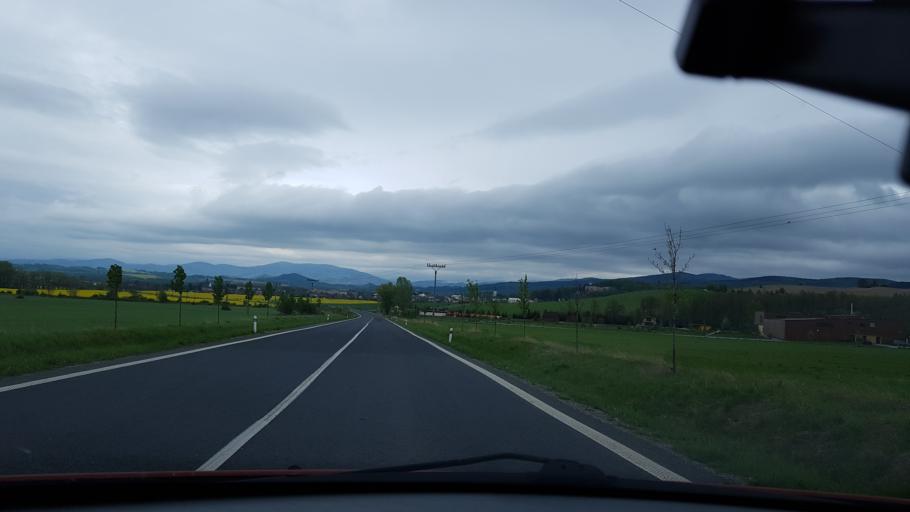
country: CZ
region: Olomoucky
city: Javornik
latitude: 50.4049
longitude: 16.9941
